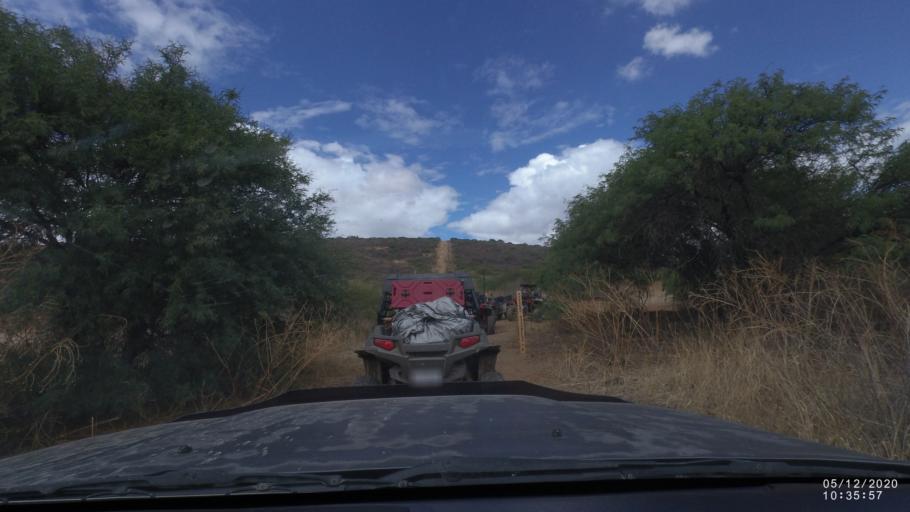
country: BO
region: Cochabamba
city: Sipe Sipe
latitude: -17.5457
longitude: -66.2792
